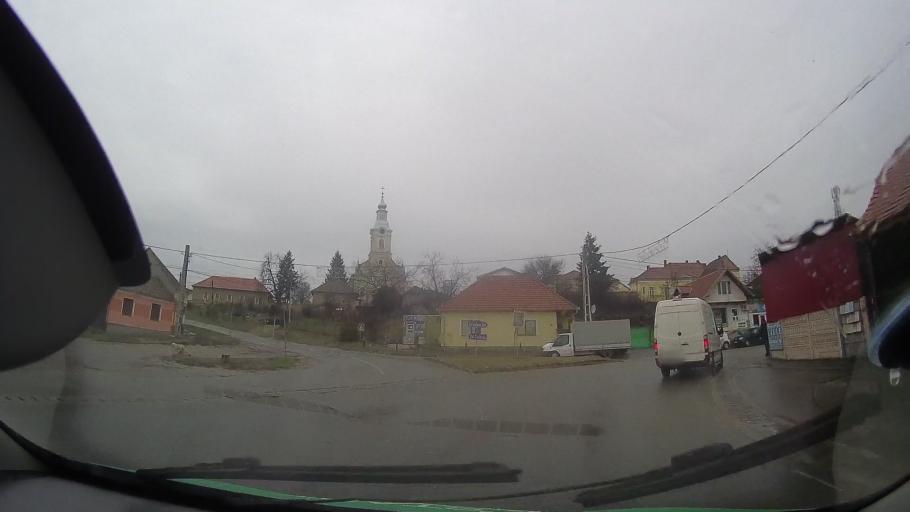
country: RO
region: Bihor
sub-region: Comuna Tinca
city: Tinca
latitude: 46.7729
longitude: 21.9300
